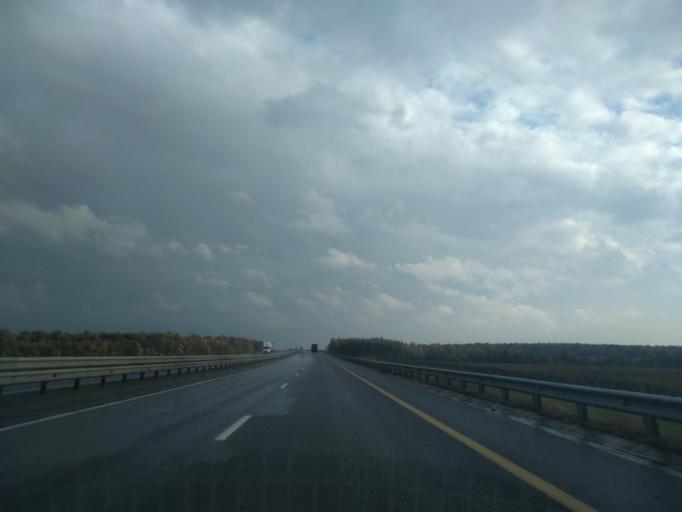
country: RU
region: Lipetsk
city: Yelets
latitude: 52.5995
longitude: 38.6699
